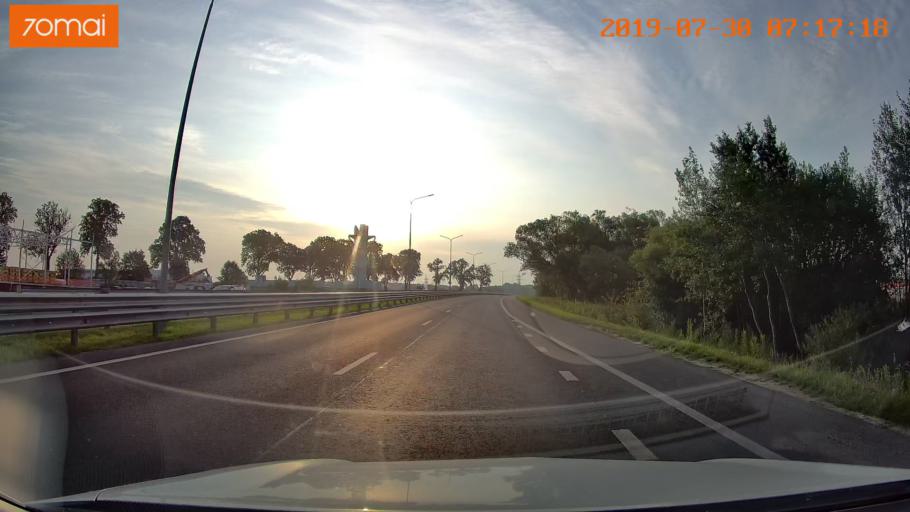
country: RU
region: Kaliningrad
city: Bol'shoe Isakovo
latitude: 54.7074
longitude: 20.6243
